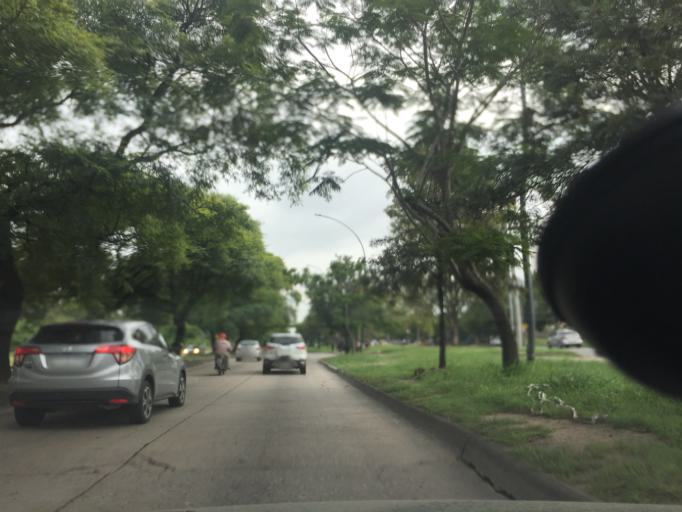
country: AR
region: Cordoba
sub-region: Departamento de Capital
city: Cordoba
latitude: -31.4366
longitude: -64.1956
